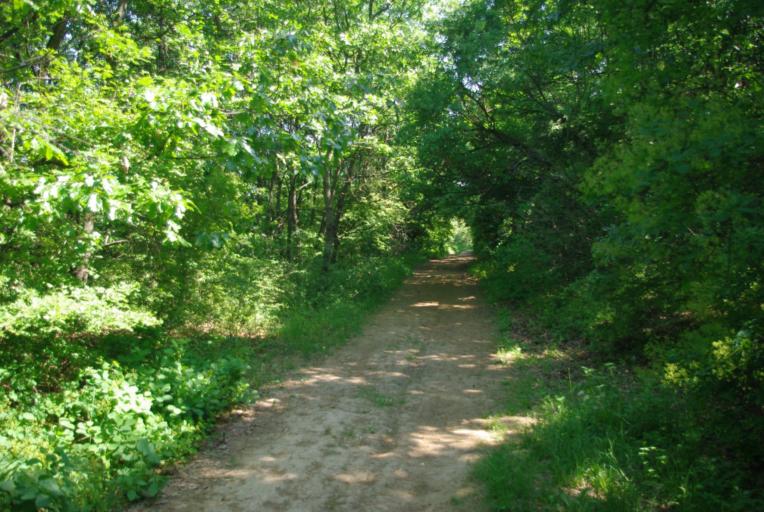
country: HU
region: Pest
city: Pilisborosjeno
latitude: 47.6098
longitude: 18.9809
